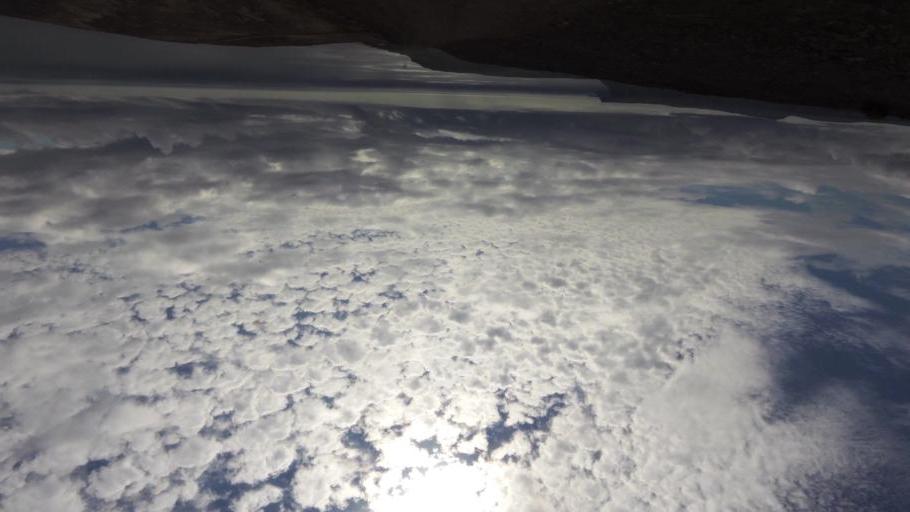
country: IS
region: West
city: Olafsvik
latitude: 65.6216
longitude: -24.3007
